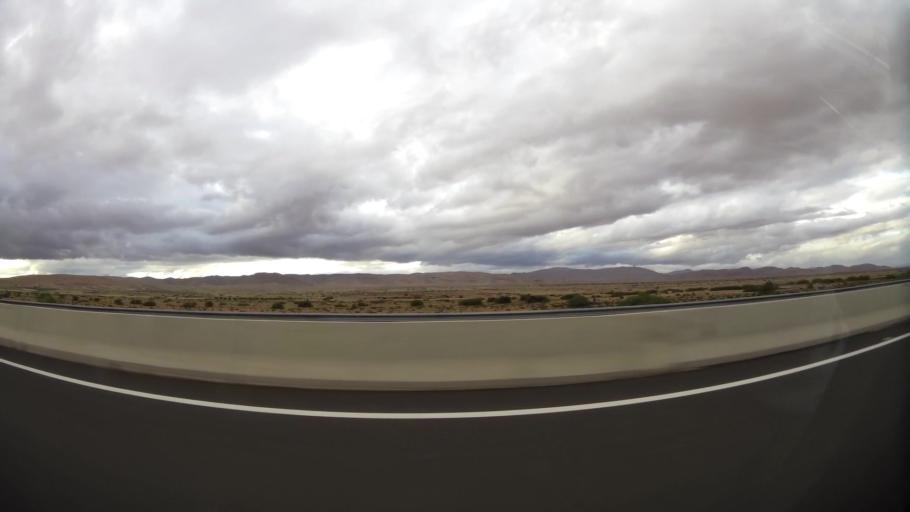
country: MA
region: Taza-Al Hoceima-Taounate
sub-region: Taza
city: Guercif
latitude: 34.3054
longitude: -3.6426
